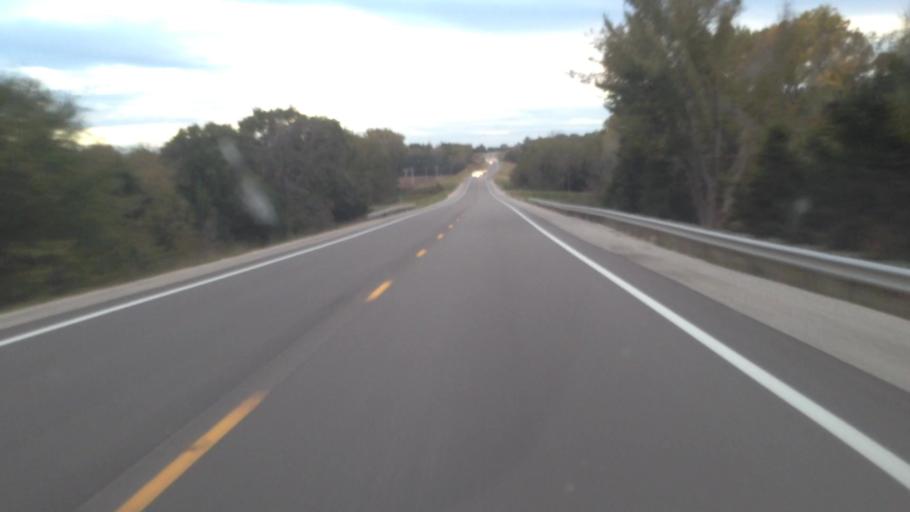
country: US
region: Kansas
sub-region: Anderson County
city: Garnett
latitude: 38.3437
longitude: -95.2488
